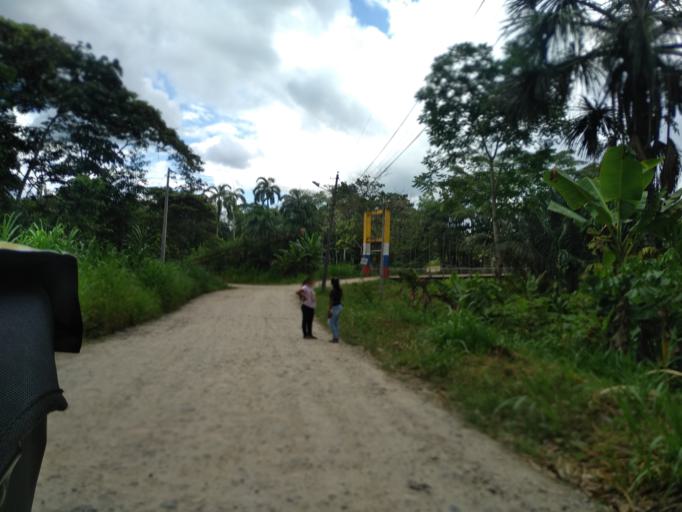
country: EC
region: Napo
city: Tena
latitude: -0.9929
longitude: -77.8197
